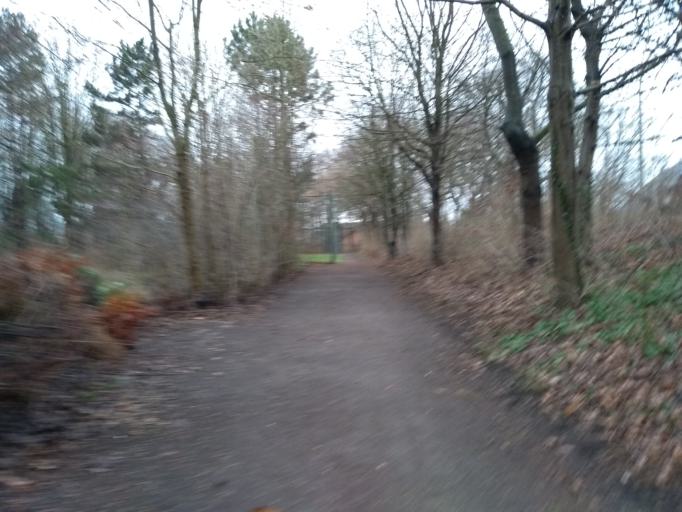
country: DE
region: North Rhine-Westphalia
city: Selm
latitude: 51.6892
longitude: 7.4587
